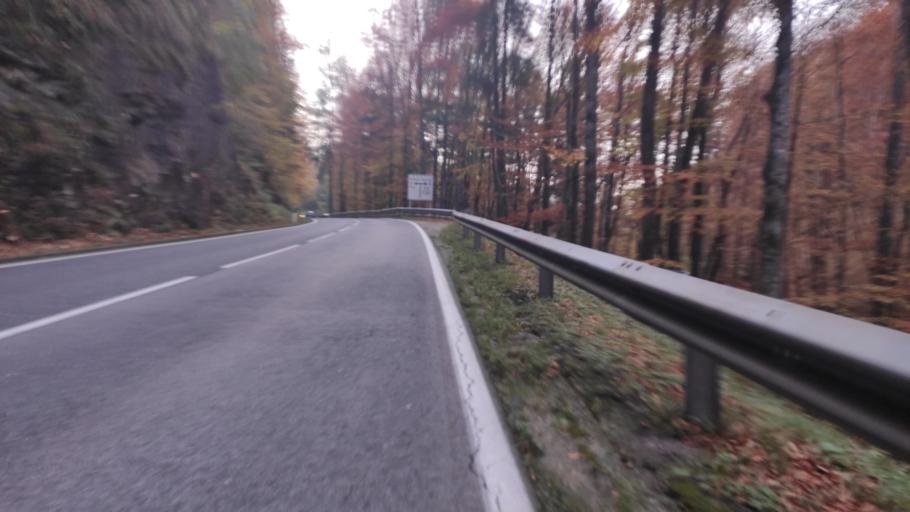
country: AT
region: Salzburg
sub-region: Politischer Bezirk Salzburg-Umgebung
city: Plainfeld
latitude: 47.8125
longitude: 13.1828
